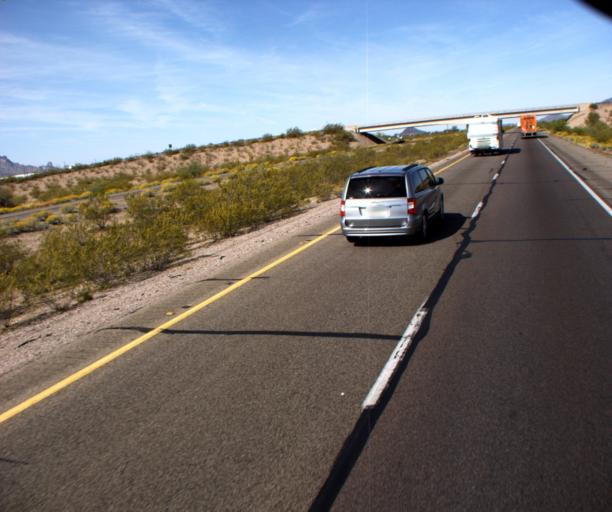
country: US
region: Arizona
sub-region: Maricopa County
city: Buckeye
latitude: 33.4970
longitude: -112.9346
